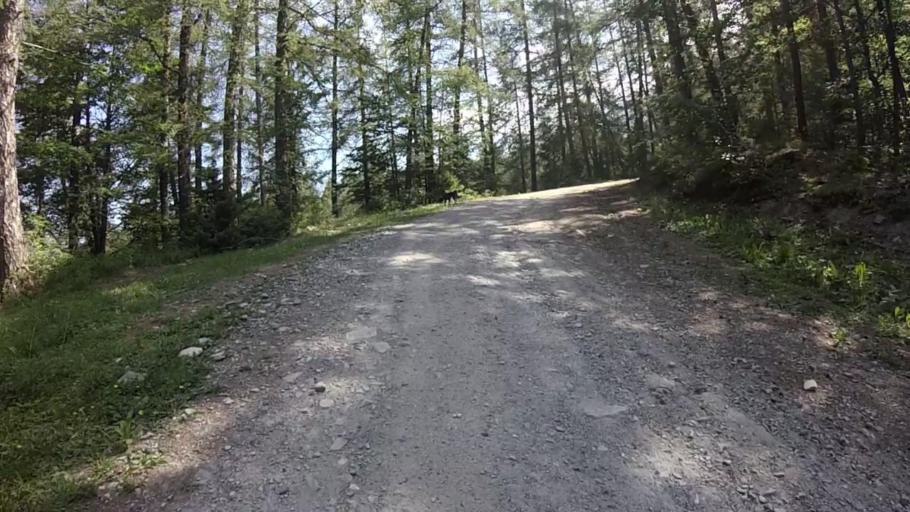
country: FR
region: Provence-Alpes-Cote d'Azur
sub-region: Departement des Alpes-de-Haute-Provence
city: Seyne-les-Alpes
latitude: 44.4048
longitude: 6.3592
